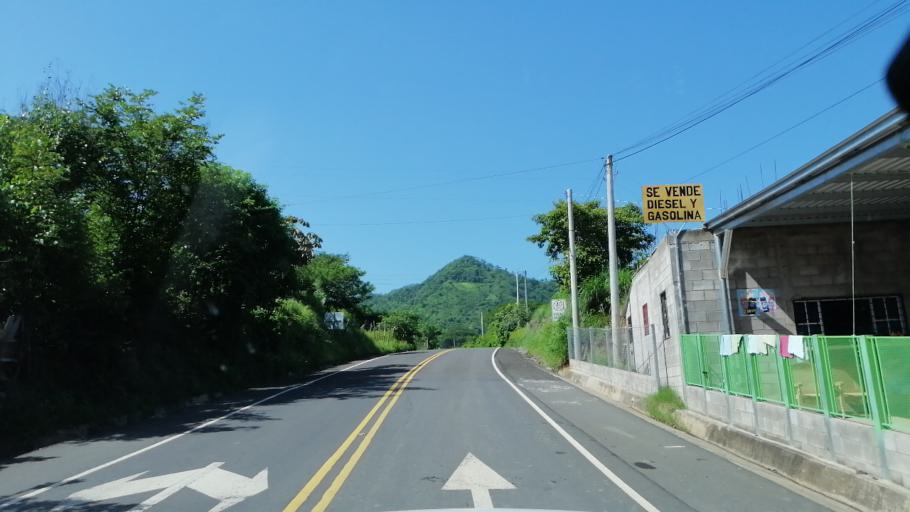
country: HN
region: Lempira
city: La Virtud
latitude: 13.9925
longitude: -88.7454
